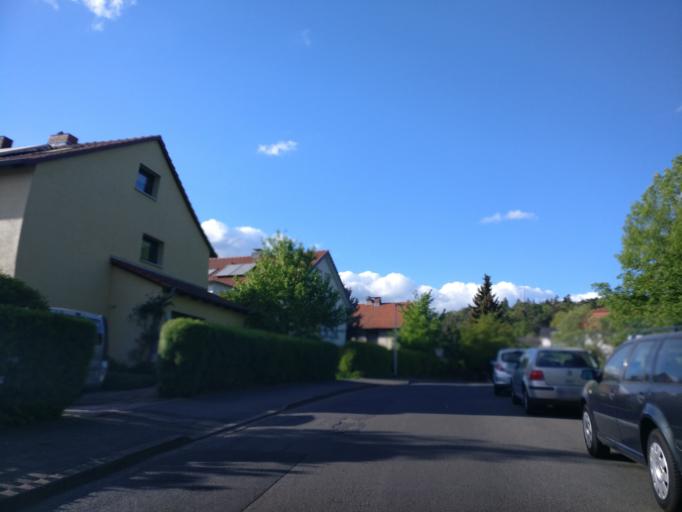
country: DE
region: Lower Saxony
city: Hannoversch Munden
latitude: 51.4034
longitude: 9.6624
